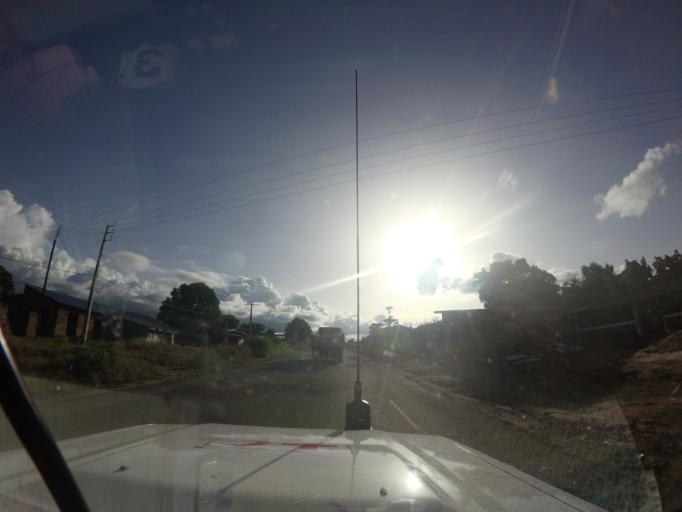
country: GN
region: Kindia
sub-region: Kindia
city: Kindia
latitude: 10.0324
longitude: -12.8565
